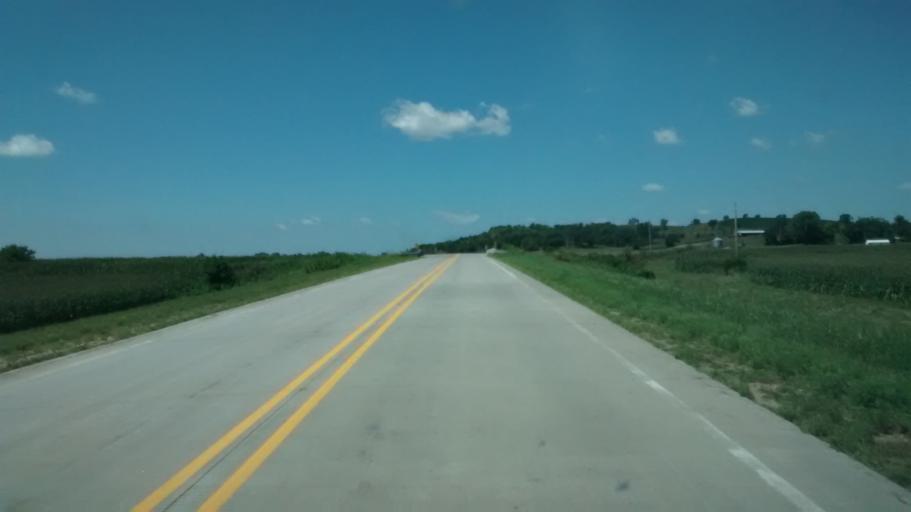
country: US
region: Iowa
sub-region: Woodbury County
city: Moville
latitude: 42.2640
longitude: -96.0518
